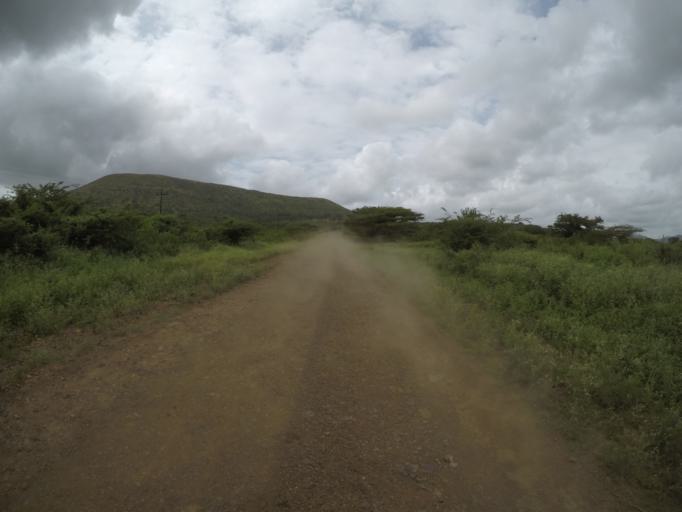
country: ZA
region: KwaZulu-Natal
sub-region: uThungulu District Municipality
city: Empangeni
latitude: -28.5970
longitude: 31.8920
